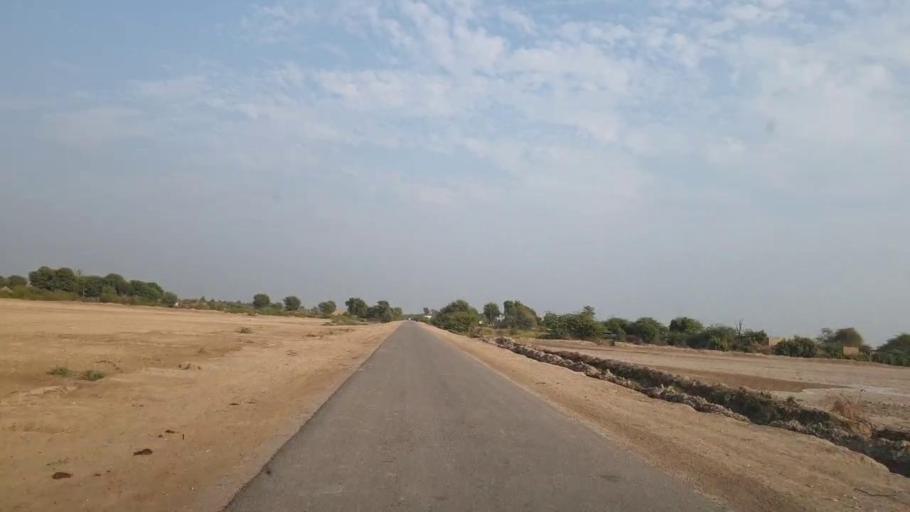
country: PK
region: Sindh
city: Pithoro
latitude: 25.5838
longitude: 69.3496
